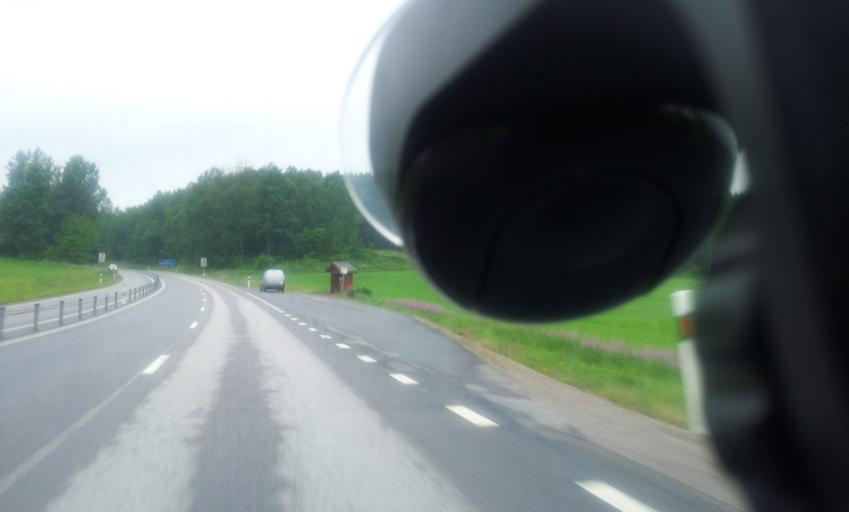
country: SE
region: Kalmar
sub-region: Vasterviks Kommun
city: Forserum
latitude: 57.9619
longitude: 16.4469
